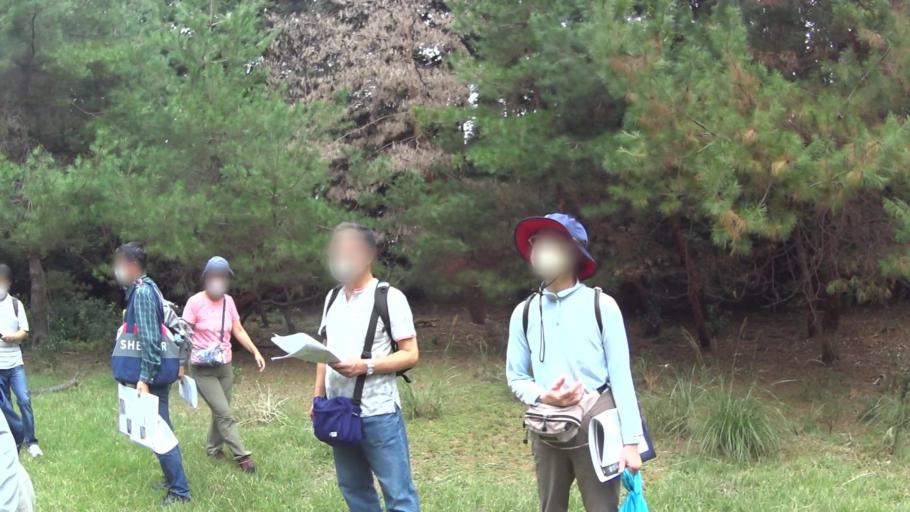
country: JP
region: Osaka
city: Kishiwada
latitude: 34.4984
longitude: 135.3310
